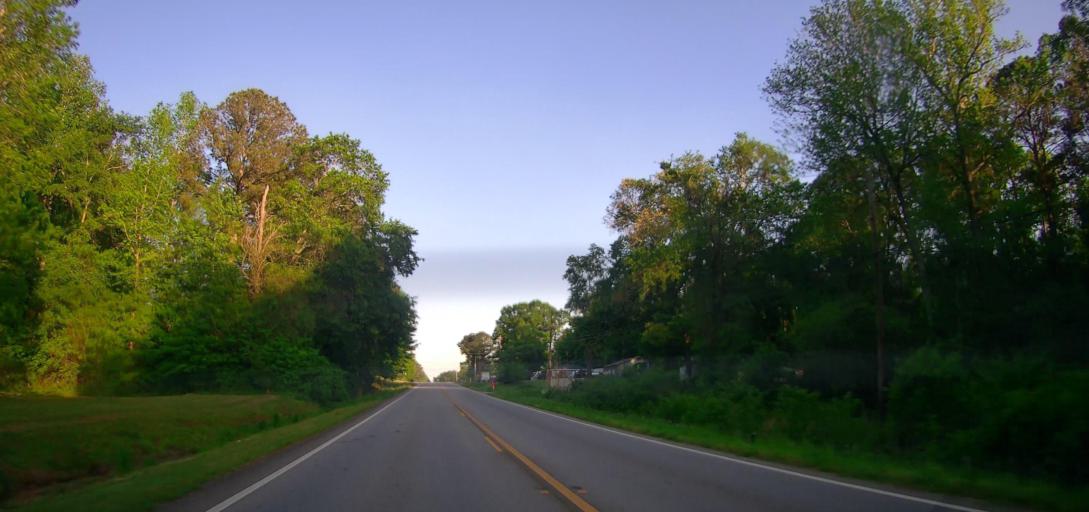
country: US
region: Georgia
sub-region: Newton County
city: Covington
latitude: 33.5770
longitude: -83.7747
